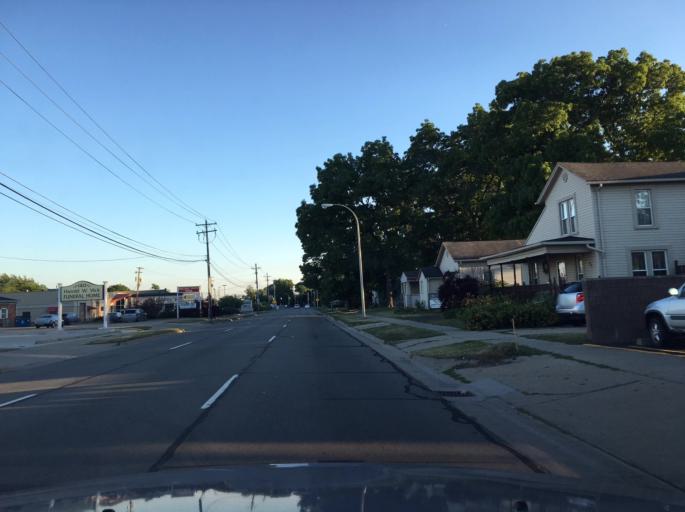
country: US
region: Michigan
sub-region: Macomb County
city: Mount Clemens
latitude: 42.5932
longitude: -82.8812
